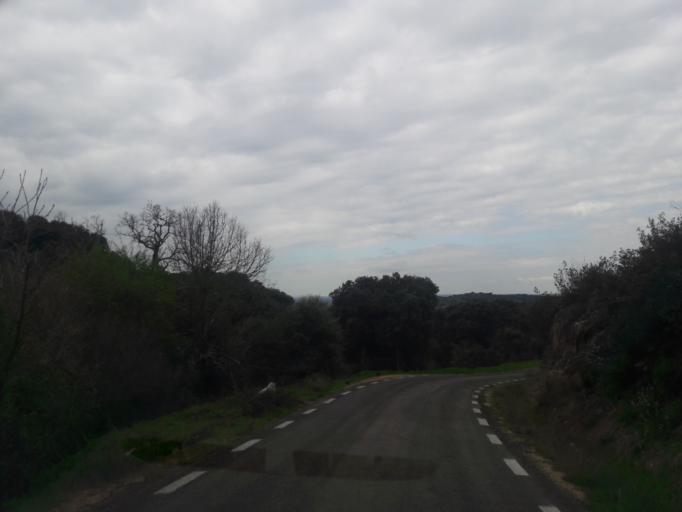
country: ES
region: Castille and Leon
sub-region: Provincia de Salamanca
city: Serradilla del Arroyo
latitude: 40.5088
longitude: -6.3997
